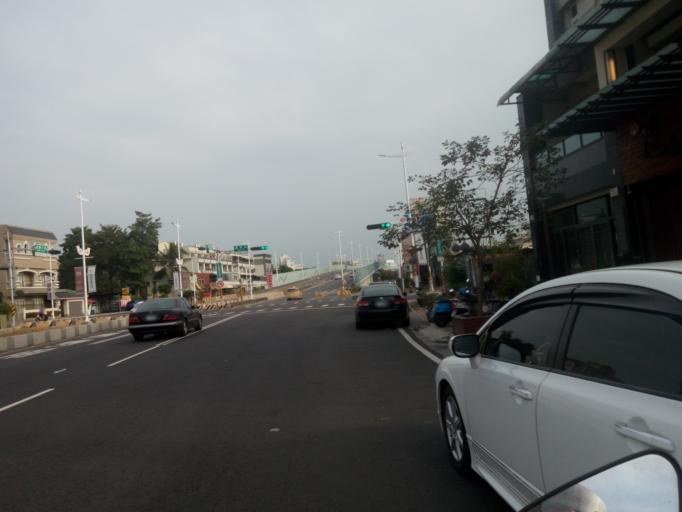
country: TW
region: Taiwan
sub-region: Chiayi
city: Jiayi Shi
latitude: 23.4775
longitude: 120.4302
